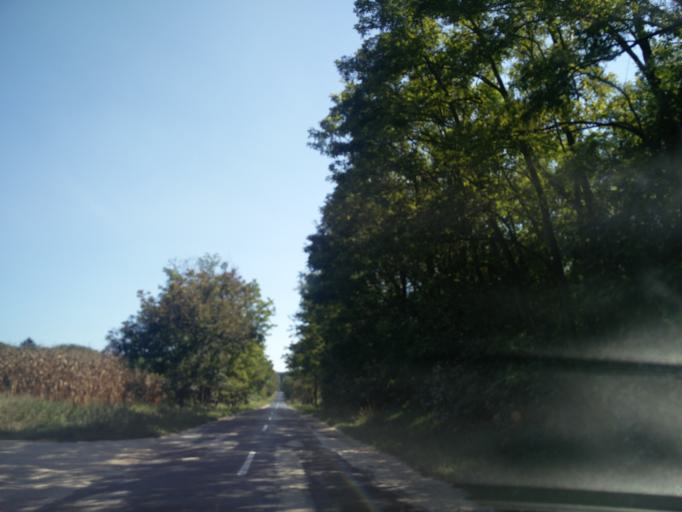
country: HU
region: Fejer
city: Lovasbereny
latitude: 47.2912
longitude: 18.5726
